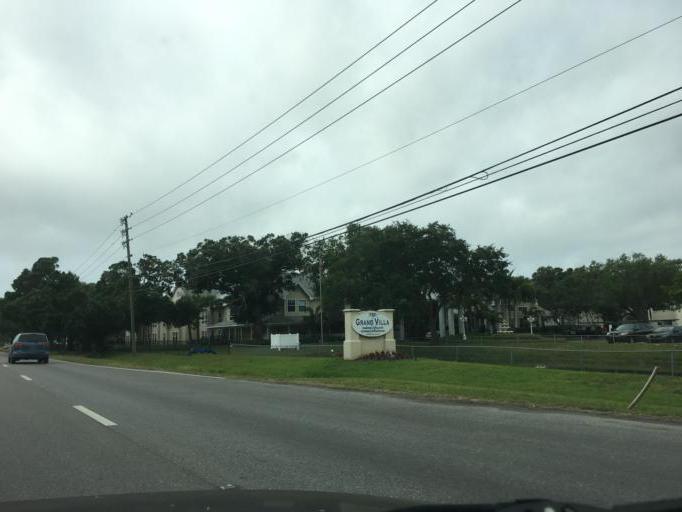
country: US
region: Florida
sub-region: Pinellas County
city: Largo
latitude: 27.9109
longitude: -82.7625
